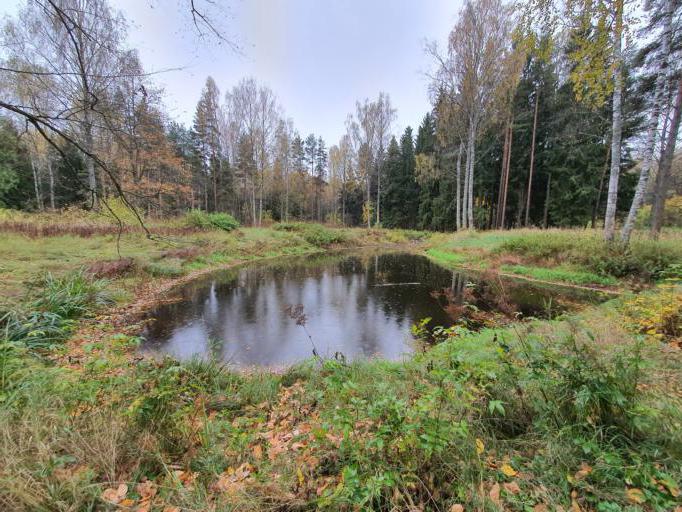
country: RU
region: St.-Petersburg
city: Tyarlevo
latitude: 59.6972
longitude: 30.4534
